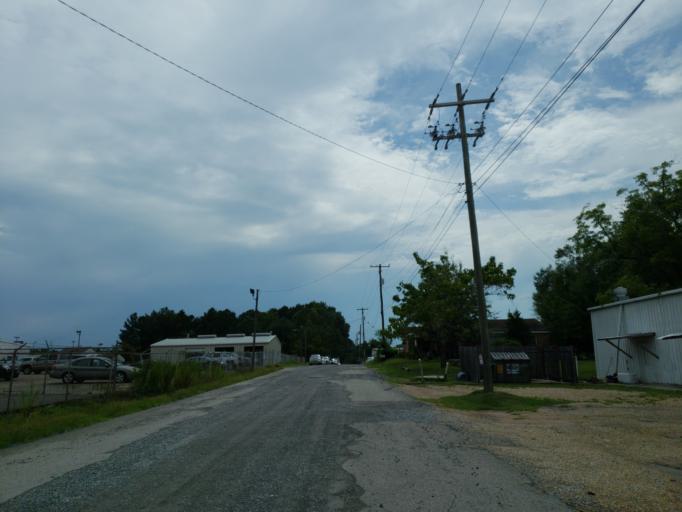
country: US
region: Mississippi
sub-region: Forrest County
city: Hattiesburg
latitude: 31.3128
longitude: -89.3084
